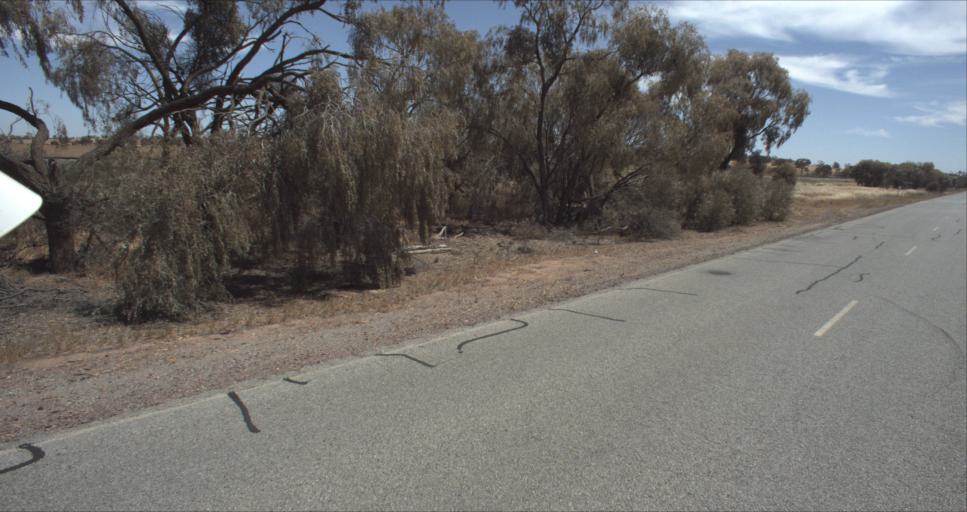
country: AU
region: New South Wales
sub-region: Leeton
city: Leeton
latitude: -34.6303
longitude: 146.4558
